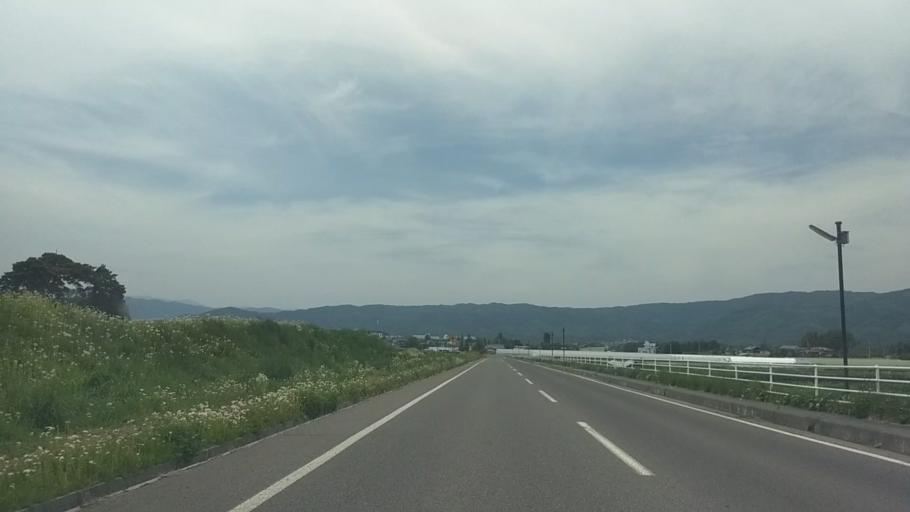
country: JP
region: Nagano
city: Chino
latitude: 36.0254
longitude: 138.2226
